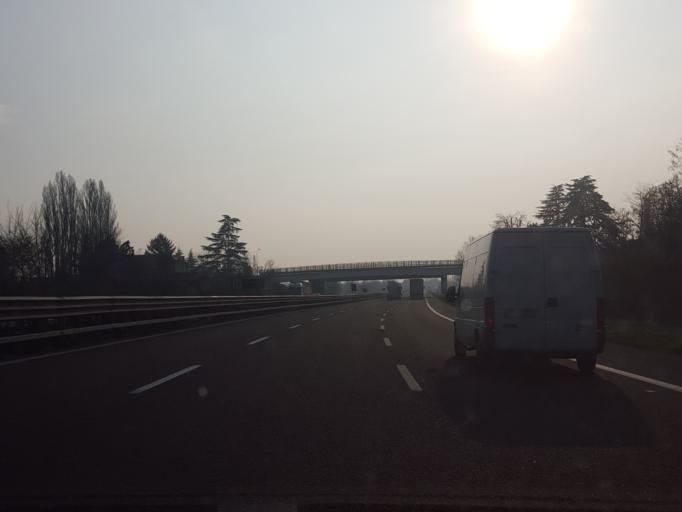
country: IT
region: Veneto
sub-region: Provincia di Treviso
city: Cendon
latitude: 45.6422
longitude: 12.3160
